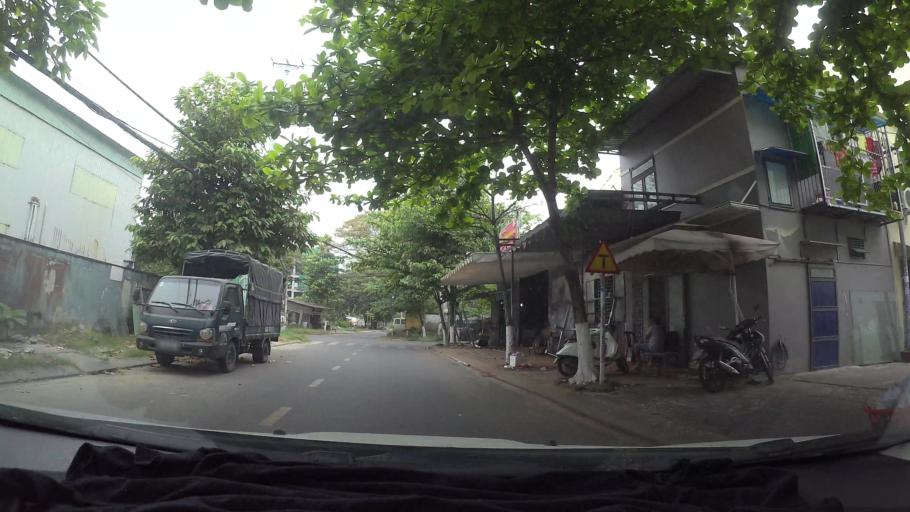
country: VN
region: Da Nang
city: Cam Le
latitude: 16.0284
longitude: 108.2093
